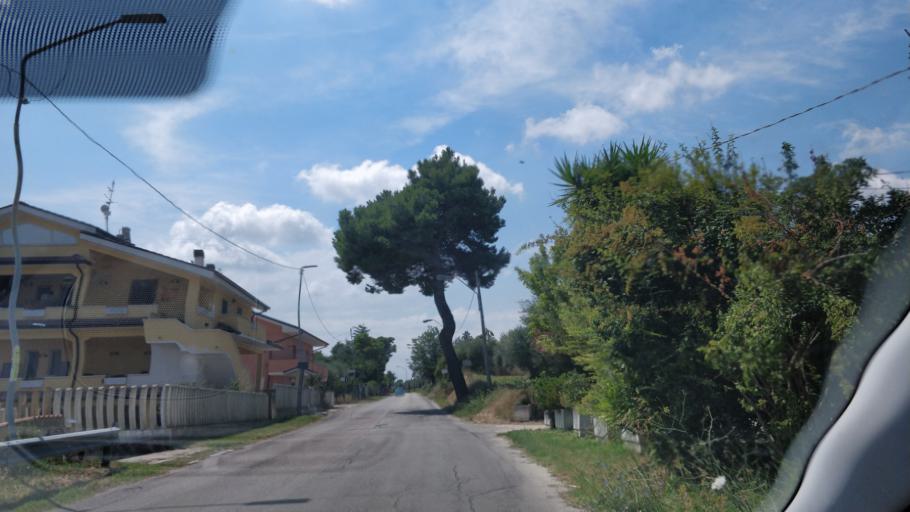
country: IT
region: Abruzzo
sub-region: Provincia di Chieti
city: Torrevecchia
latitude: 42.4024
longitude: 14.2154
